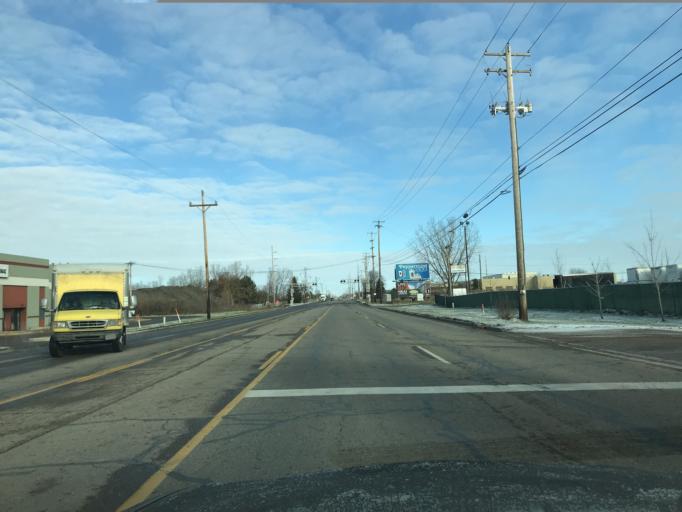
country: US
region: Michigan
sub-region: Eaton County
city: Dimondale
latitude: 42.6891
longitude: -84.6423
